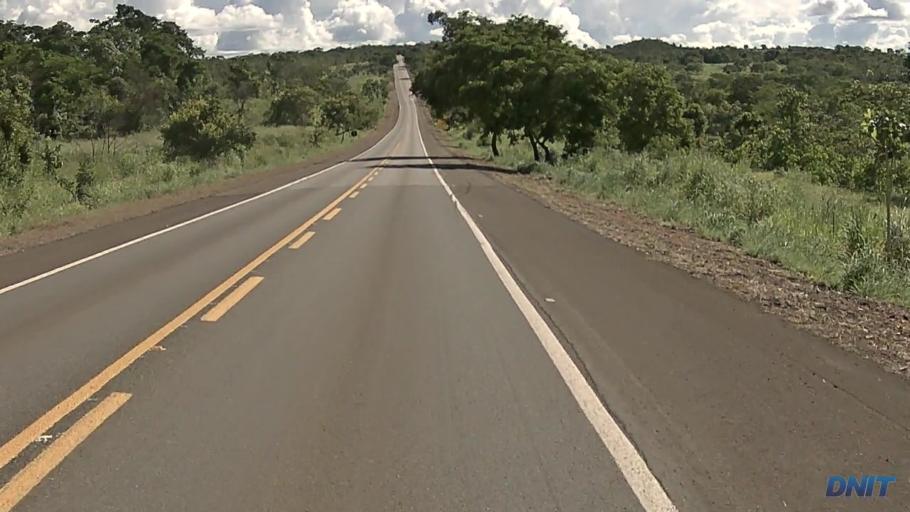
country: BR
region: Goias
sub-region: Padre Bernardo
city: Padre Bernardo
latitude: -15.1839
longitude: -48.4304
